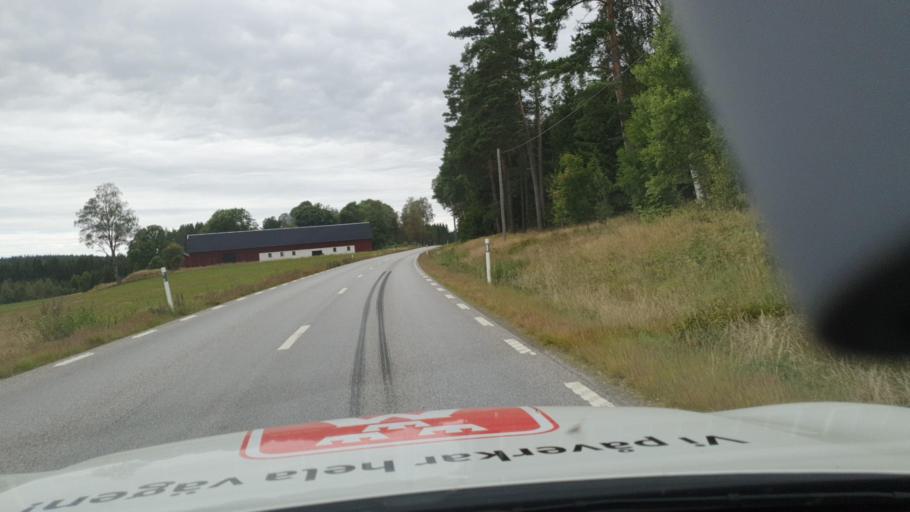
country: SE
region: Vaestra Goetaland
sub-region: Dals-Ed Kommun
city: Ed
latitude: 58.8803
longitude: 11.9881
